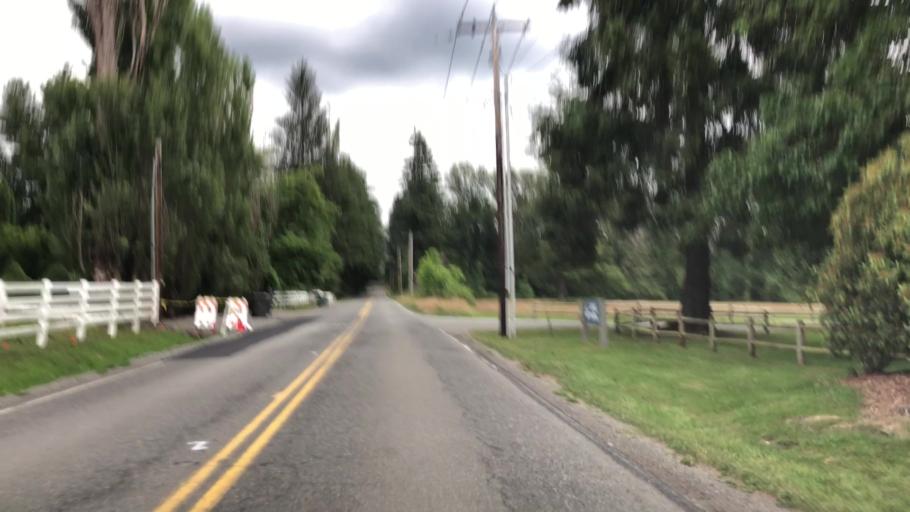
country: US
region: Washington
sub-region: King County
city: Redmond
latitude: 47.7028
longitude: -122.0897
